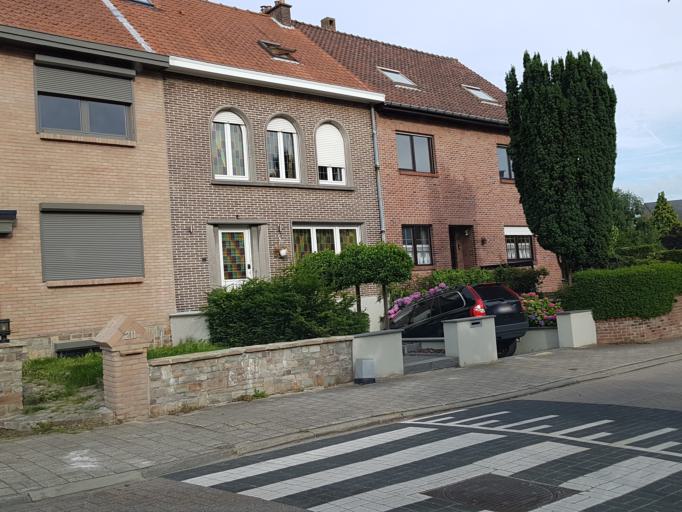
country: BE
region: Flanders
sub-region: Provincie Vlaams-Brabant
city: Kraainem
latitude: 50.8517
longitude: 4.4620
